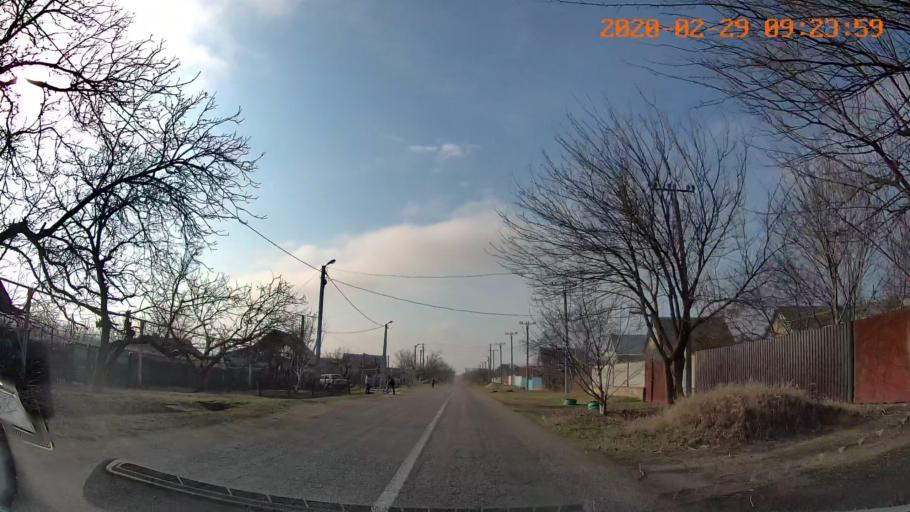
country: MD
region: Telenesti
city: Pervomaisc
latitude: 46.7205
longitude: 29.9598
